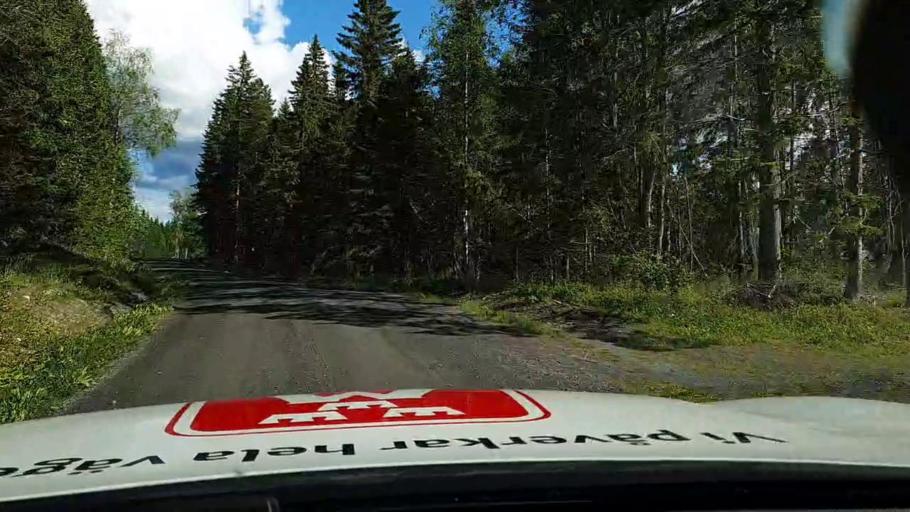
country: SE
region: Jaemtland
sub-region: Krokoms Kommun
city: Valla
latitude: 63.3184
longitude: 13.7664
